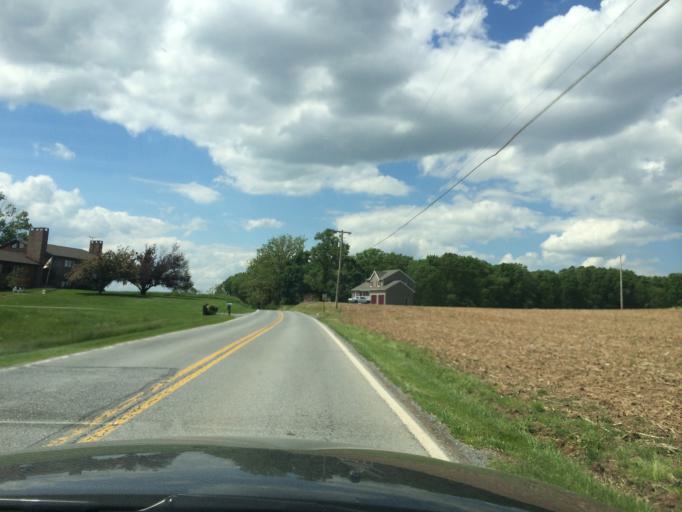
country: US
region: Maryland
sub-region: Frederick County
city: Woodsboro
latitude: 39.5377
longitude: -77.2324
